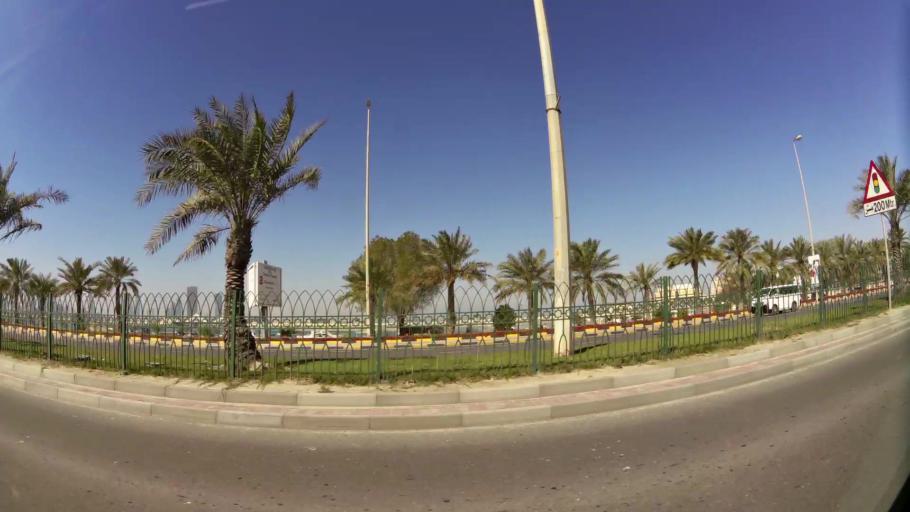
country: BH
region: Muharraq
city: Al Muharraq
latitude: 26.2581
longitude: 50.6033
